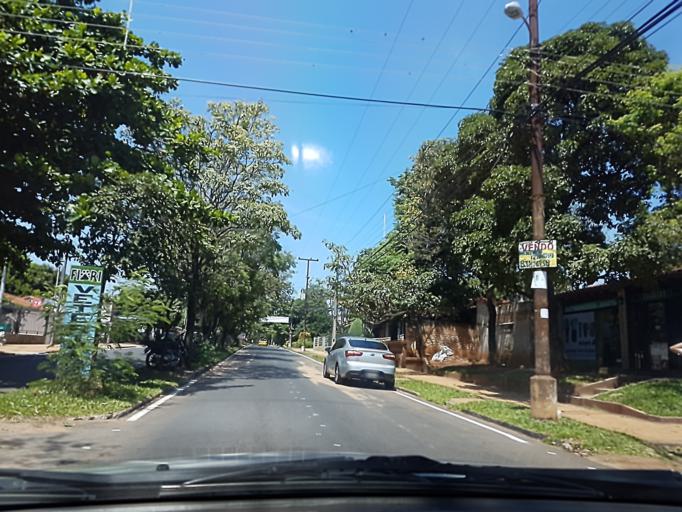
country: PY
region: Central
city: Fernando de la Mora
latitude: -25.2867
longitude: -57.5245
